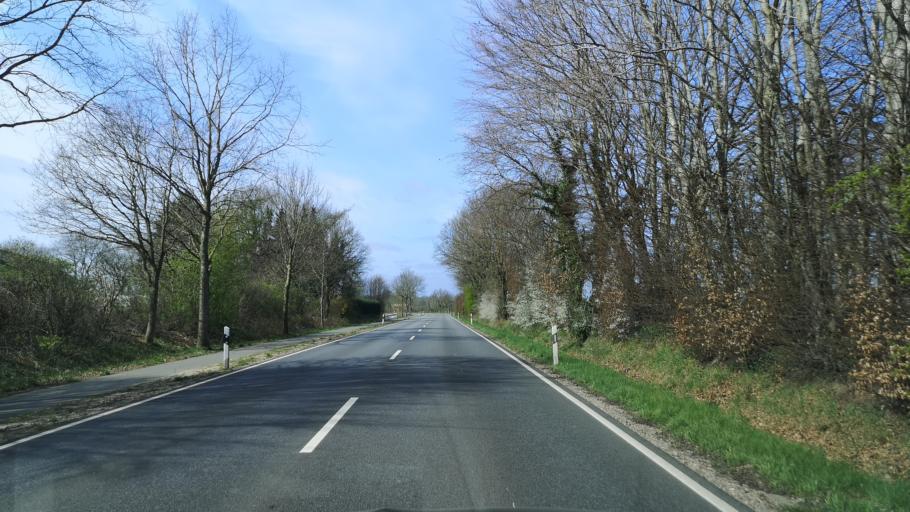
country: DE
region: Schleswig-Holstein
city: Hamdorf
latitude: 54.2275
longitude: 9.5092
